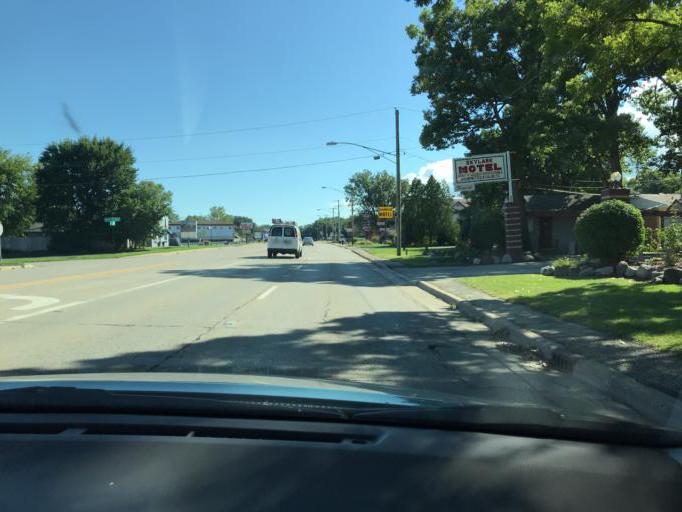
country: US
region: Illinois
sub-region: Lake County
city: Winthrop Harbor
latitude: 42.4775
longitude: -87.8240
